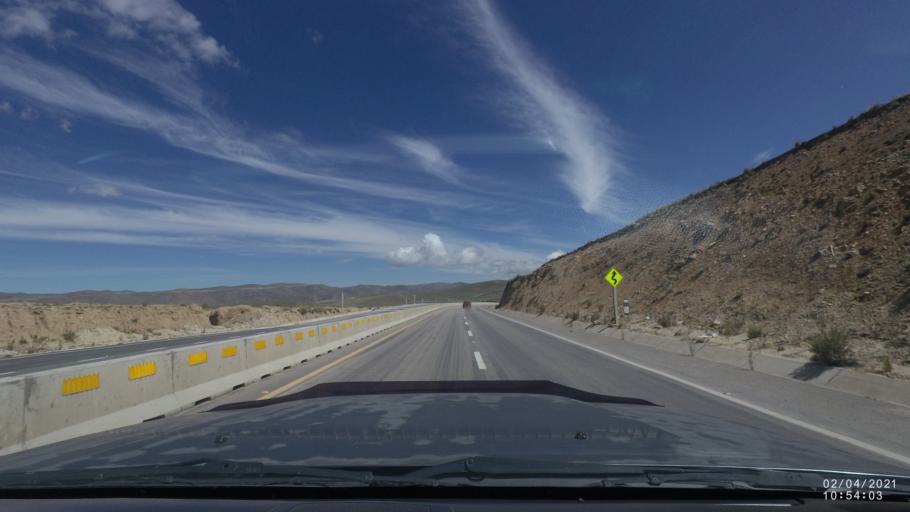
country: BO
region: Cochabamba
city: Colchani
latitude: -17.6680
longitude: -66.7523
